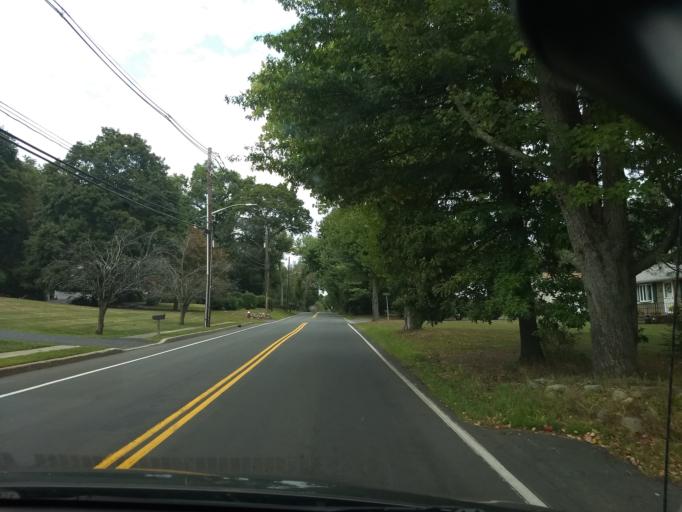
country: US
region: New York
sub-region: Rockland County
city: Nanuet
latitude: 41.0907
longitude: -74.0345
